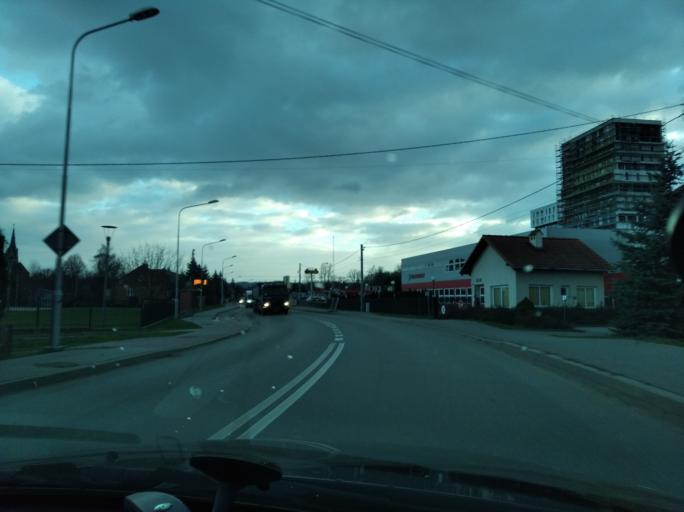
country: PL
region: Subcarpathian Voivodeship
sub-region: Rzeszow
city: Rzeszow
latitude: 50.0304
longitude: 22.0417
